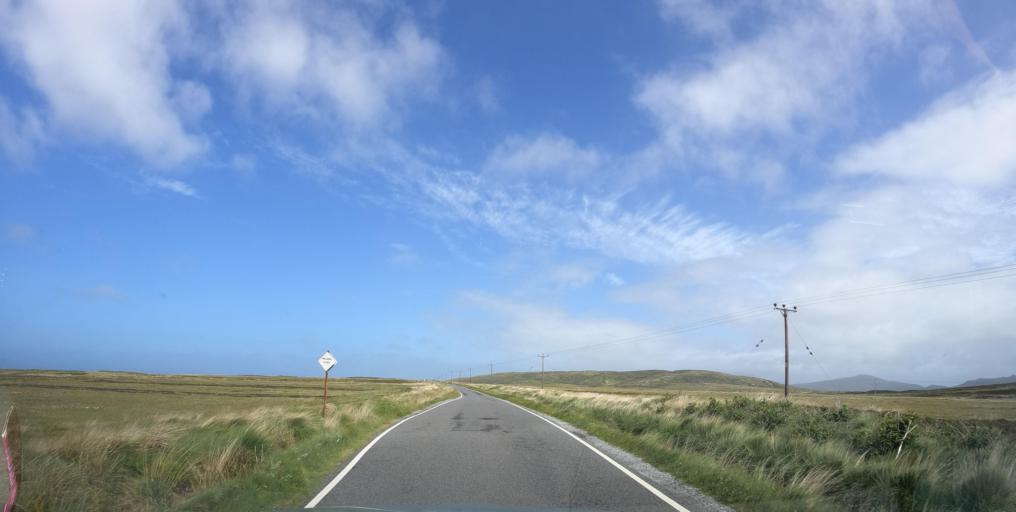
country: GB
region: Scotland
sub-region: Eilean Siar
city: Isle of South Uist
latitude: 57.1315
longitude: -7.3615
